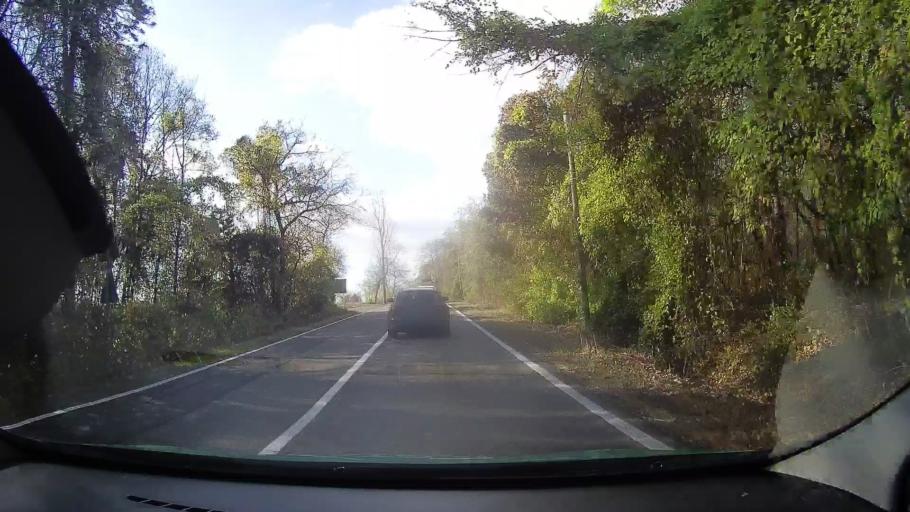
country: RO
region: Tulcea
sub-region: Comuna Topolog
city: Topolog
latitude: 44.9072
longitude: 28.4097
